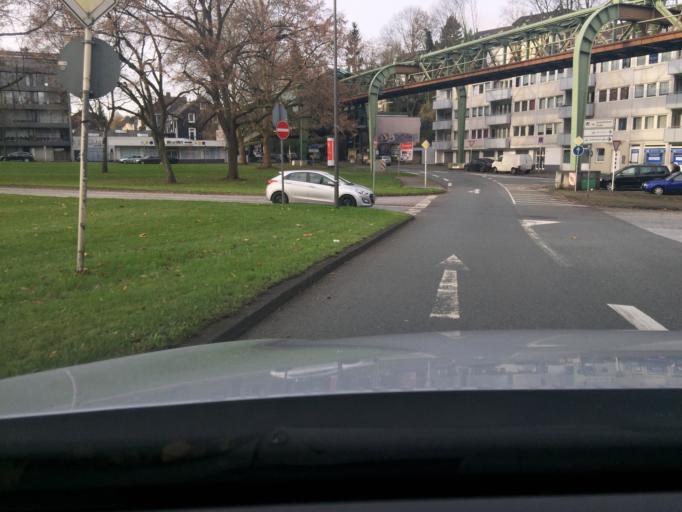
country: DE
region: North Rhine-Westphalia
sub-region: Regierungsbezirk Dusseldorf
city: Solingen
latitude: 51.2366
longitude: 7.0898
